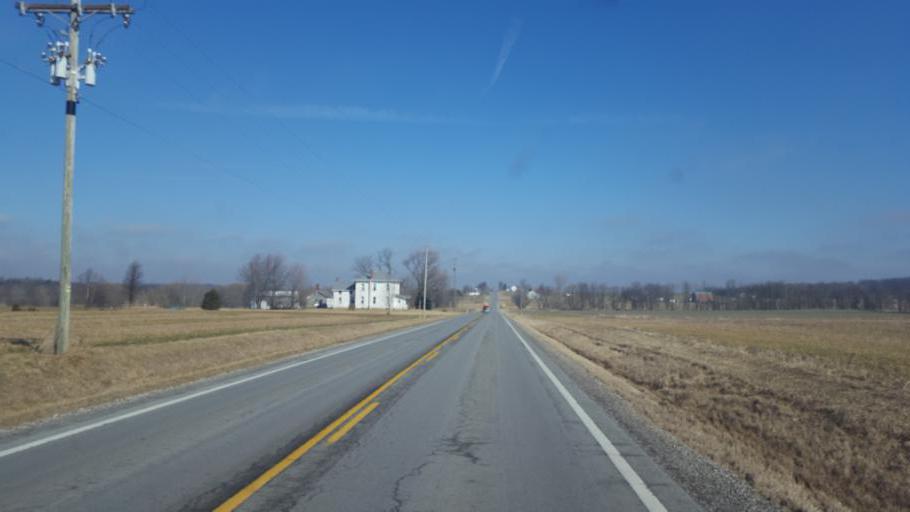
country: US
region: Ohio
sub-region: Crawford County
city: Bucyrus
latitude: 40.8929
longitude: -82.9581
